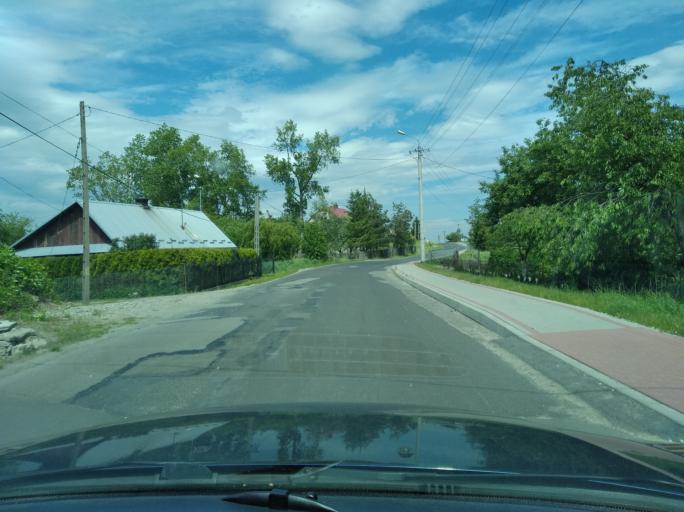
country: PL
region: Subcarpathian Voivodeship
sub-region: Powiat ropczycko-sedziszowski
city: Ropczyce
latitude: 50.0309
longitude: 21.6128
